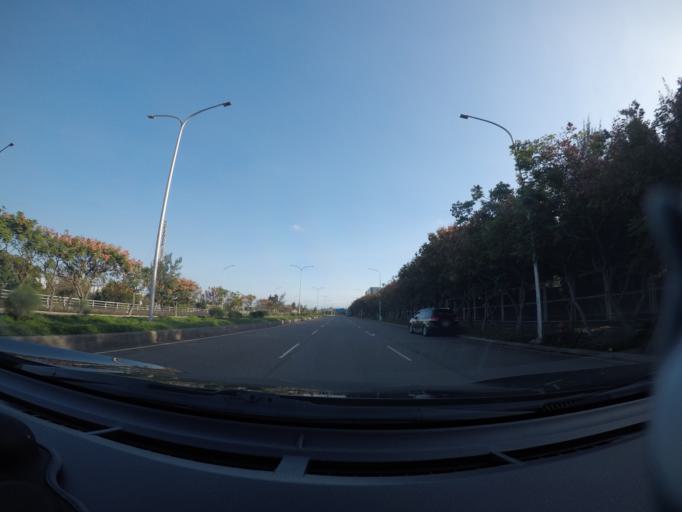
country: TW
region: Taiwan
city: Taoyuan City
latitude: 25.0985
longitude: 121.2555
